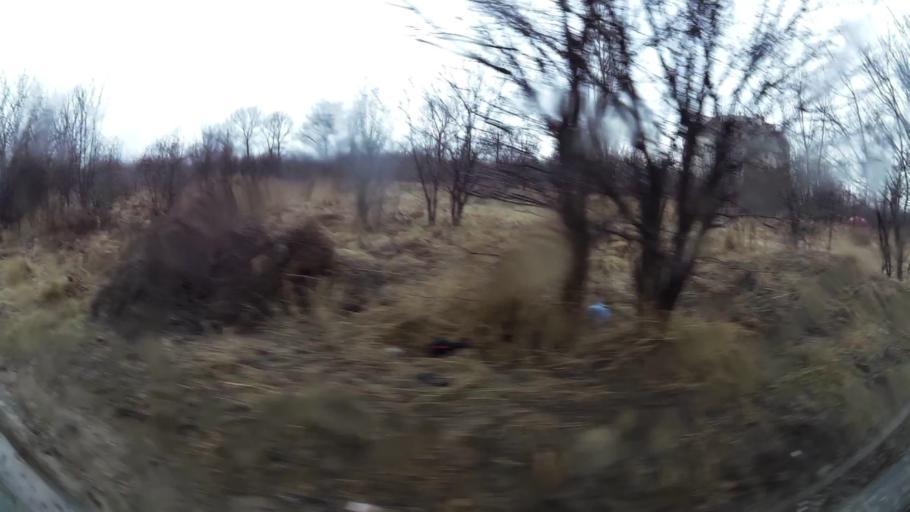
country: BG
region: Sofia-Capital
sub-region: Stolichna Obshtina
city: Sofia
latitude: 42.6510
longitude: 23.3291
